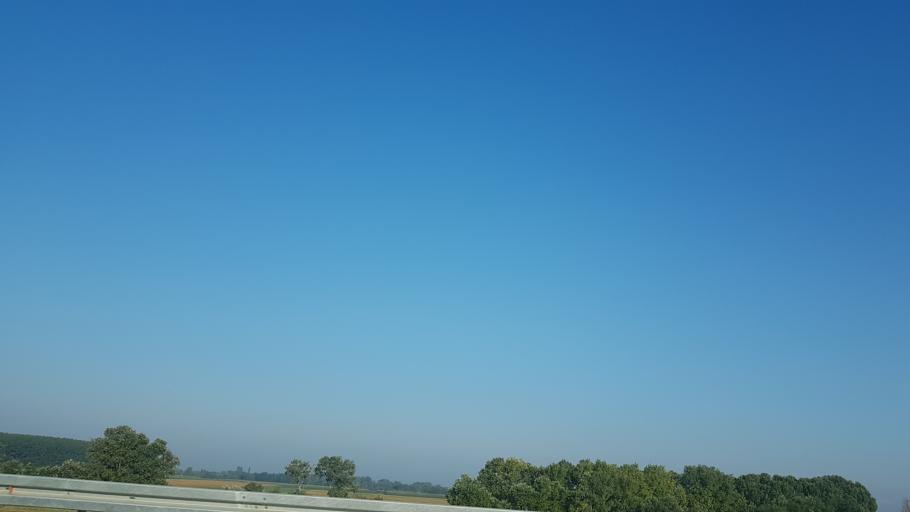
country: TR
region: Bursa
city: Karacabey
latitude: 40.1530
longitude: 28.3105
